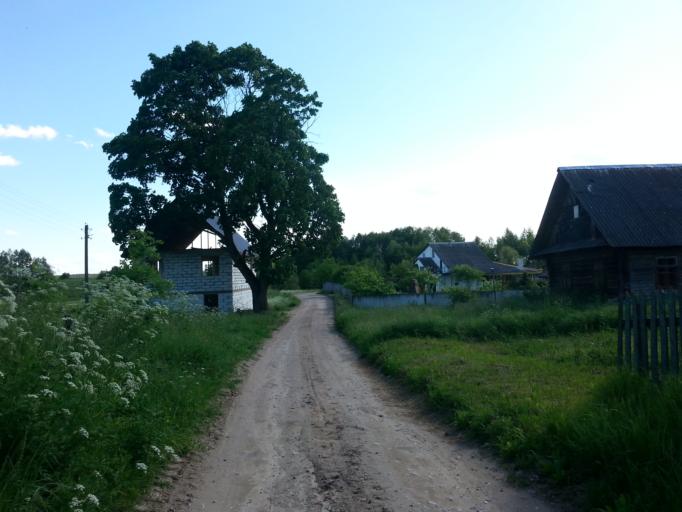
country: BY
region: Minsk
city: Narach
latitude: 54.9765
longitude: 26.6137
